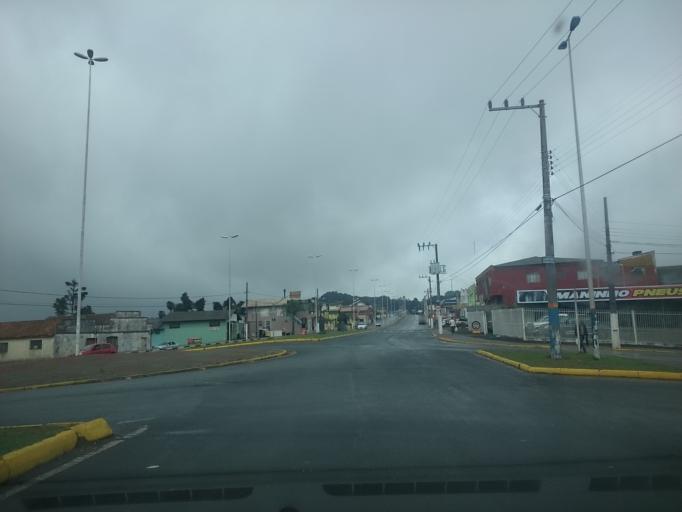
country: BR
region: Santa Catarina
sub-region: Lages
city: Lages
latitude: -27.8287
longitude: -50.3379
